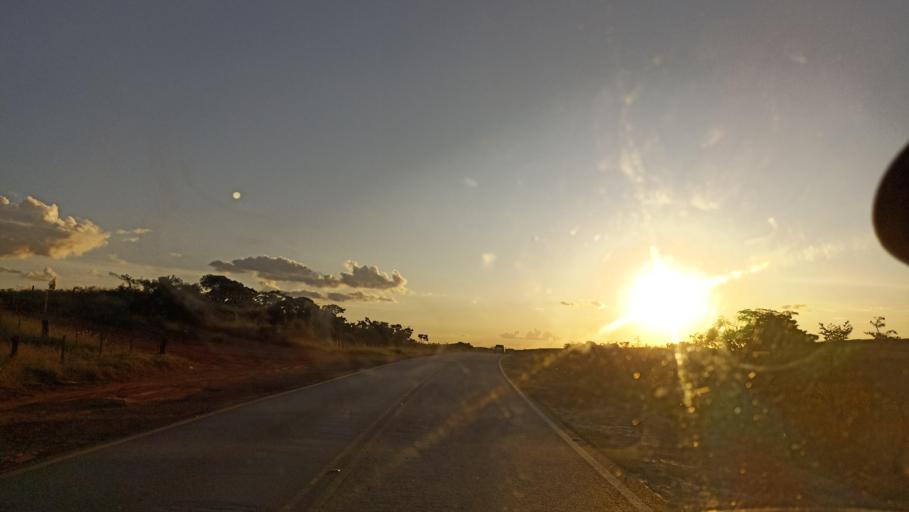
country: BR
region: Minas Gerais
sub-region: Sao Joao Del Rei
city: Sao Joao del Rei
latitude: -21.2254
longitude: -44.3663
